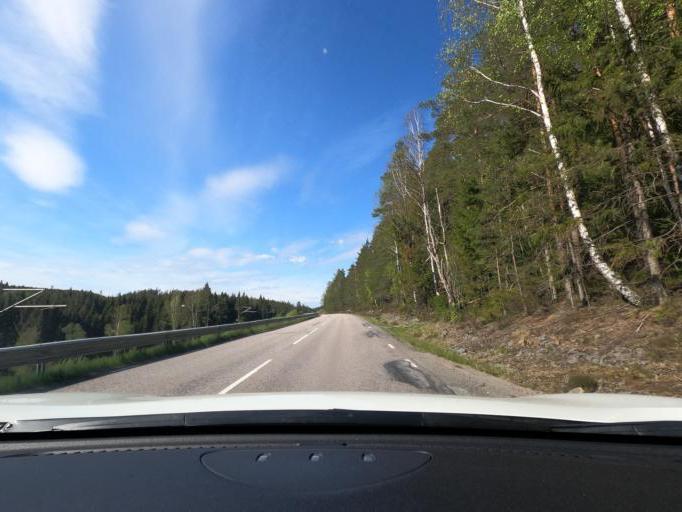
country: SE
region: Vaestra Goetaland
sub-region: Harryda Kommun
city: Ravlanda
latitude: 57.6627
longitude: 12.4855
